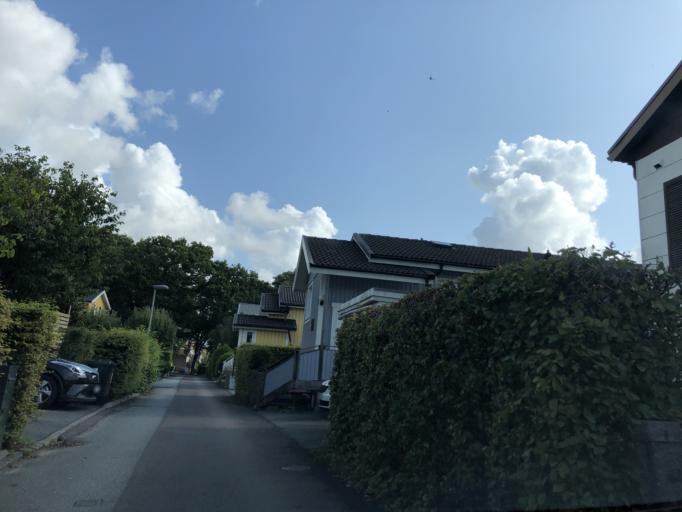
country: SE
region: Vaestra Goetaland
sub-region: Goteborg
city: Majorna
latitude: 57.7044
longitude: 11.8996
